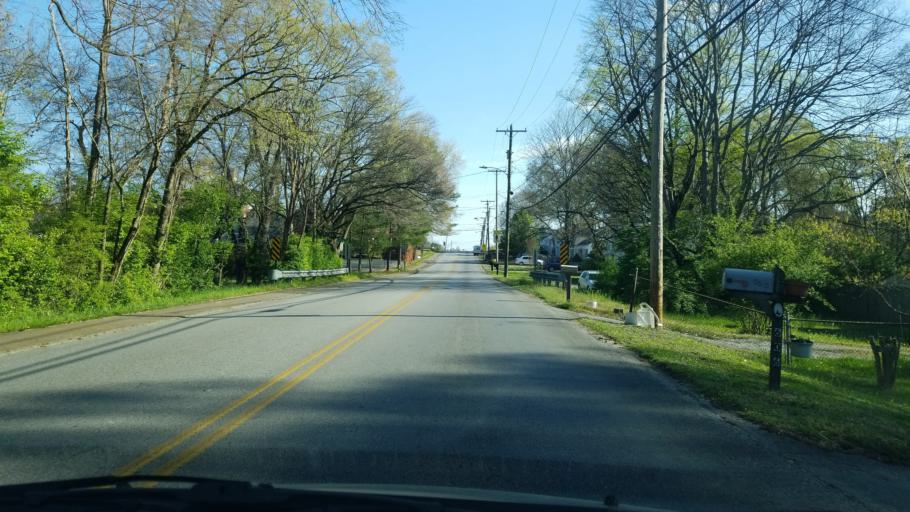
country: US
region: Tennessee
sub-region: Hamilton County
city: East Ridge
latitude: 35.0032
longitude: -85.2335
